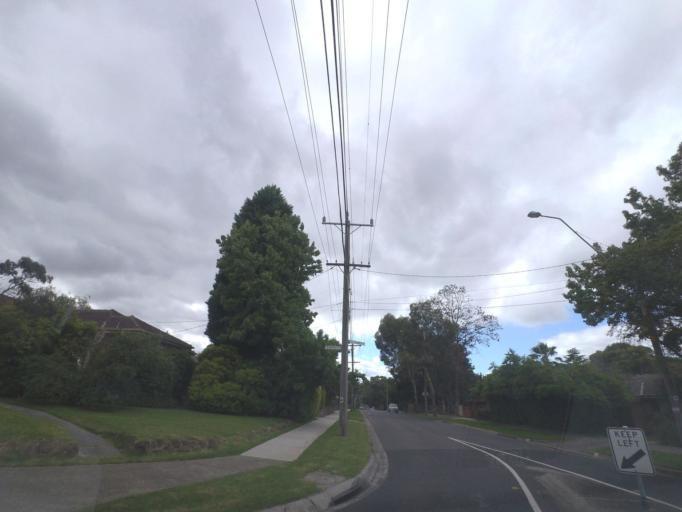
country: AU
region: Victoria
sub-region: Whitehorse
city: Vermont
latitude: -37.8306
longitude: 145.2087
